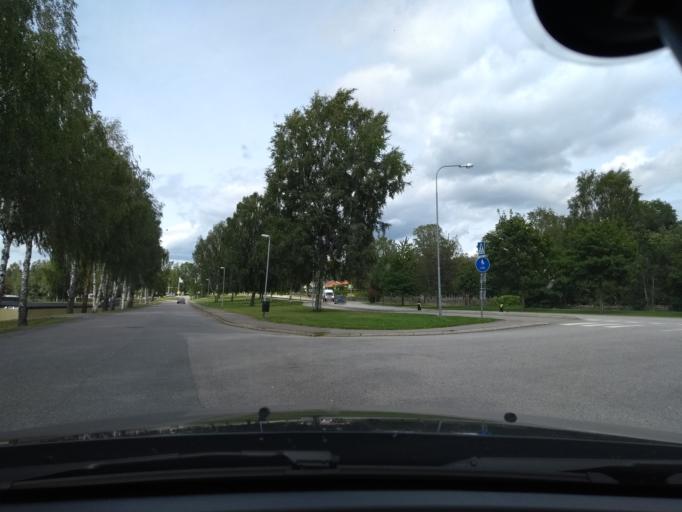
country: SE
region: Kalmar
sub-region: Vimmerby Kommun
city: Vimmerby
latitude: 57.6749
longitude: 15.8550
